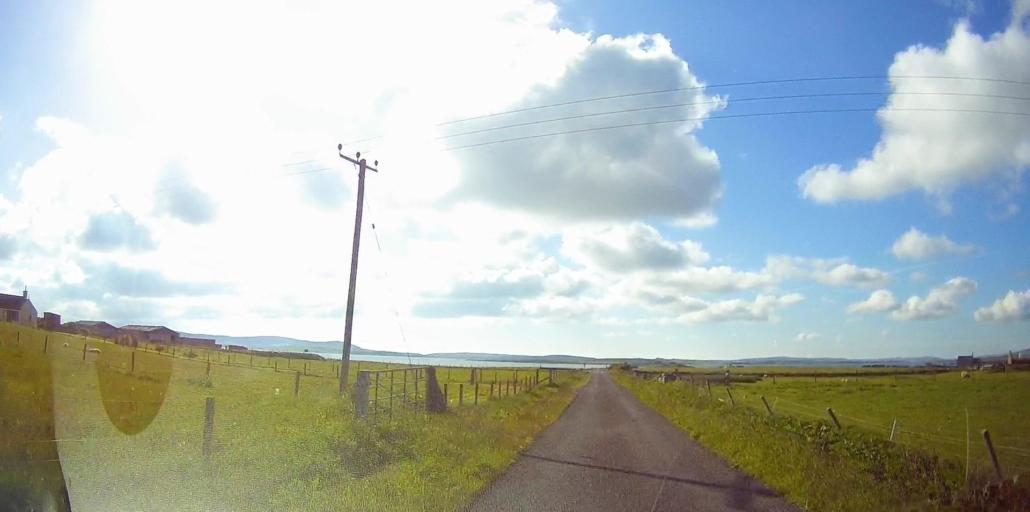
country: GB
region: Scotland
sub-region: Orkney Islands
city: Stromness
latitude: 58.9887
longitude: -3.1976
